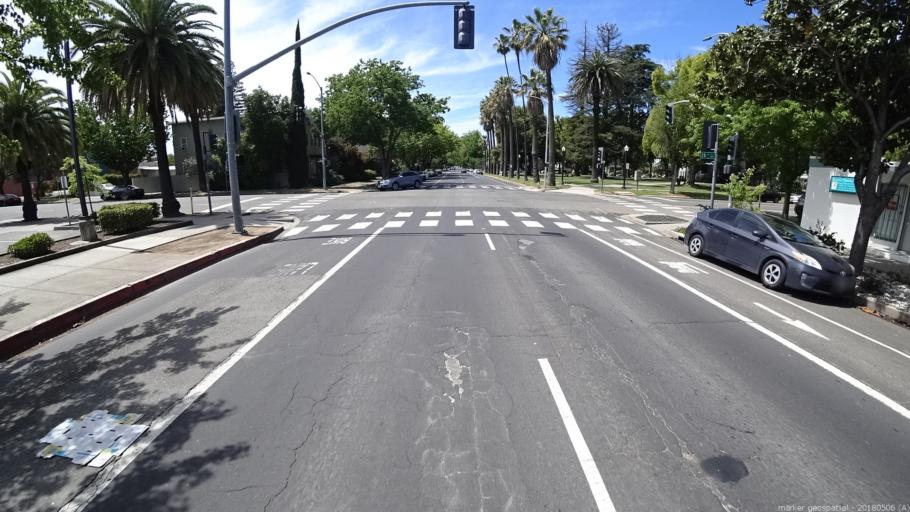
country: US
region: California
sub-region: Sacramento County
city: Sacramento
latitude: 38.5661
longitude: -121.4724
